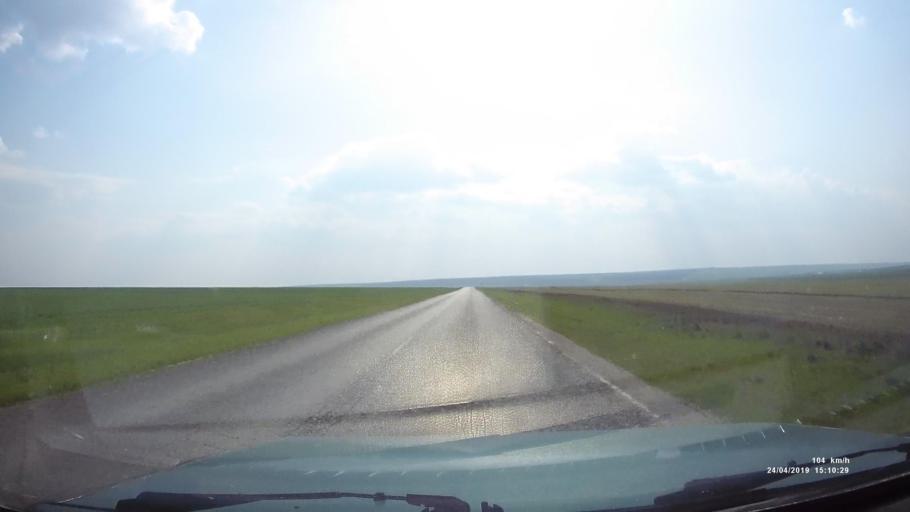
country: RU
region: Rostov
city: Remontnoye
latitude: 46.5494
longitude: 43.3405
